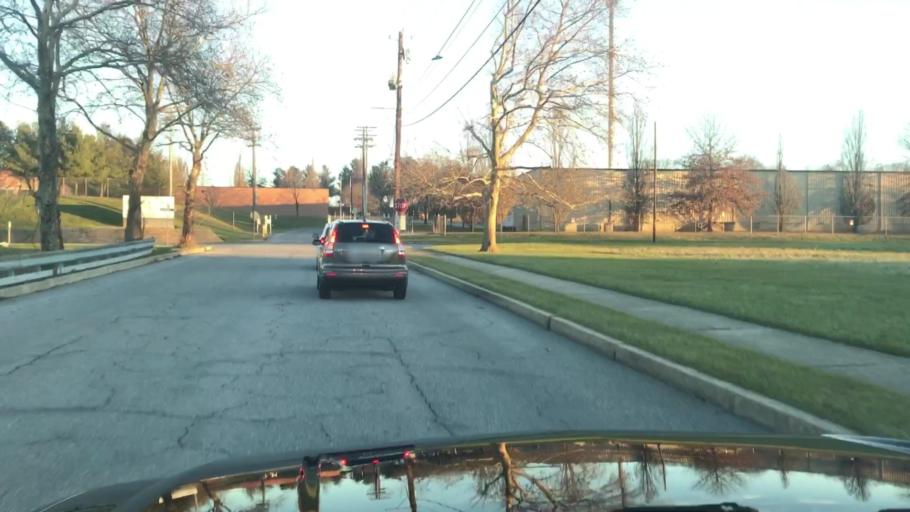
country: US
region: Pennsylvania
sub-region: Dauphin County
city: Harrisburg
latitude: 40.2796
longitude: -76.8690
